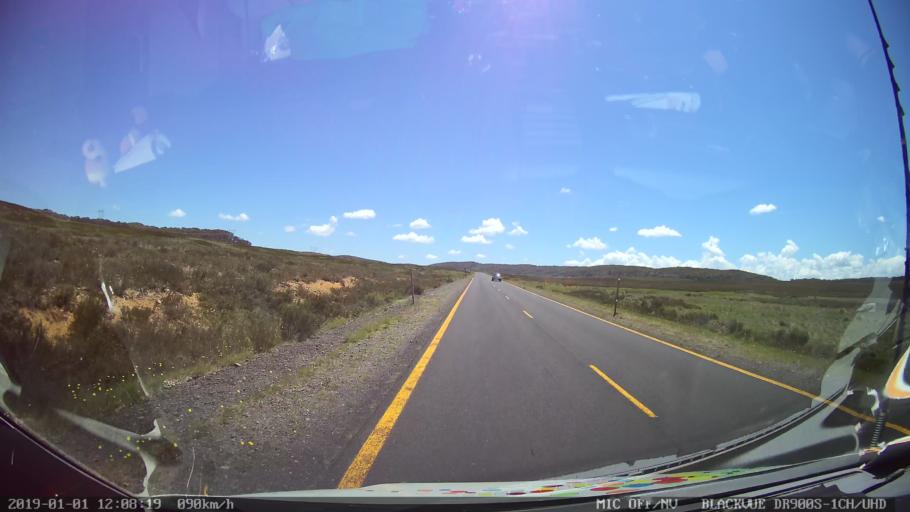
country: AU
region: New South Wales
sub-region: Tumut Shire
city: Tumut
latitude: -35.8219
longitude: 148.4941
